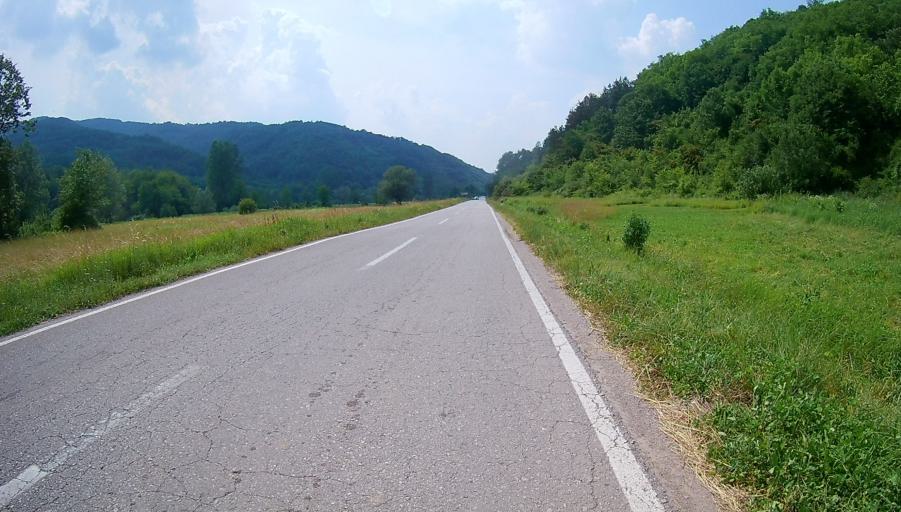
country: RS
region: Central Serbia
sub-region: Nisavski Okrug
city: Gadzin Han
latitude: 43.1652
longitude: 22.0962
